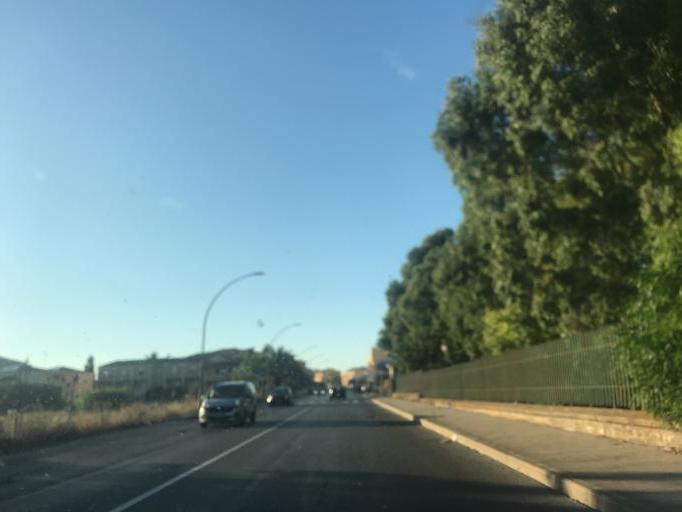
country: IT
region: Sardinia
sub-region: Provincia di Sassari
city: Alghero
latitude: 40.5805
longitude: 8.3186
